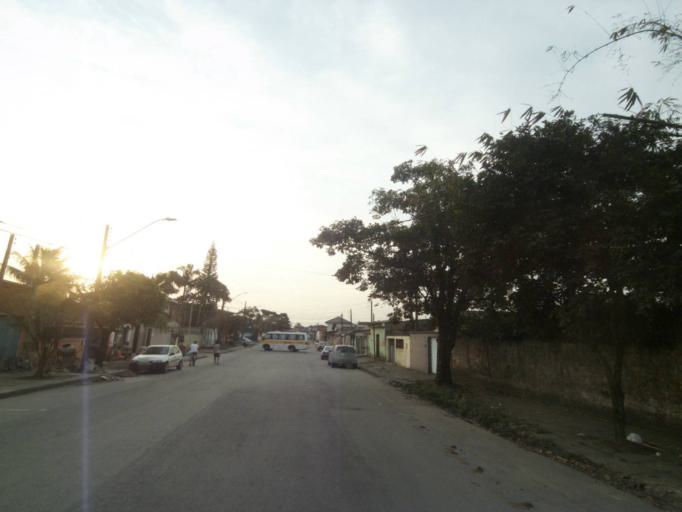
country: BR
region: Parana
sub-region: Paranagua
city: Paranagua
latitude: -25.5190
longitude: -48.5393
